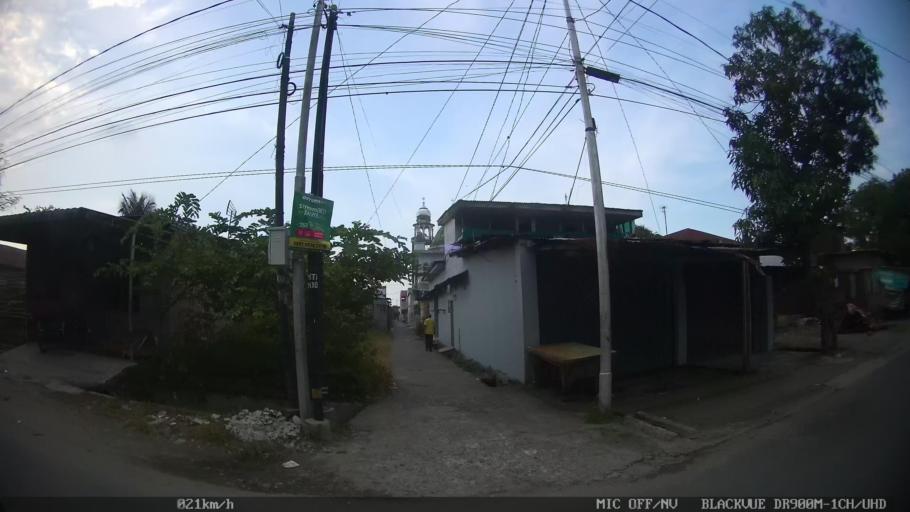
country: ID
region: North Sumatra
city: Medan
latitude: 3.6099
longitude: 98.6875
